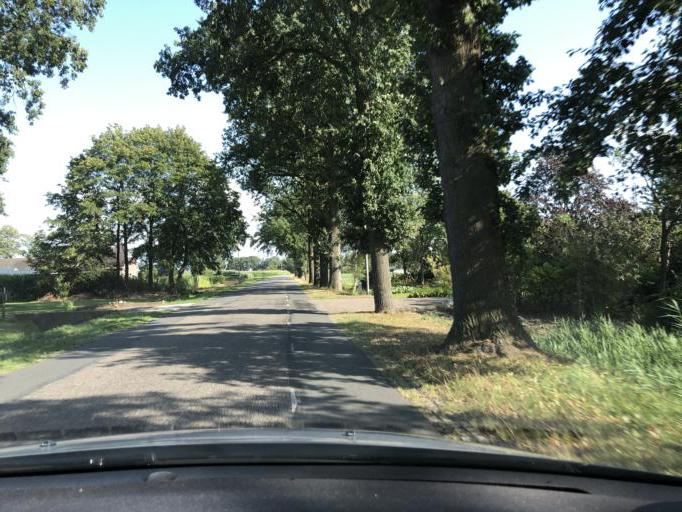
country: NL
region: Overijssel
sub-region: Gemeente Staphorst
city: Staphorst
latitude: 52.6069
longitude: 6.2764
